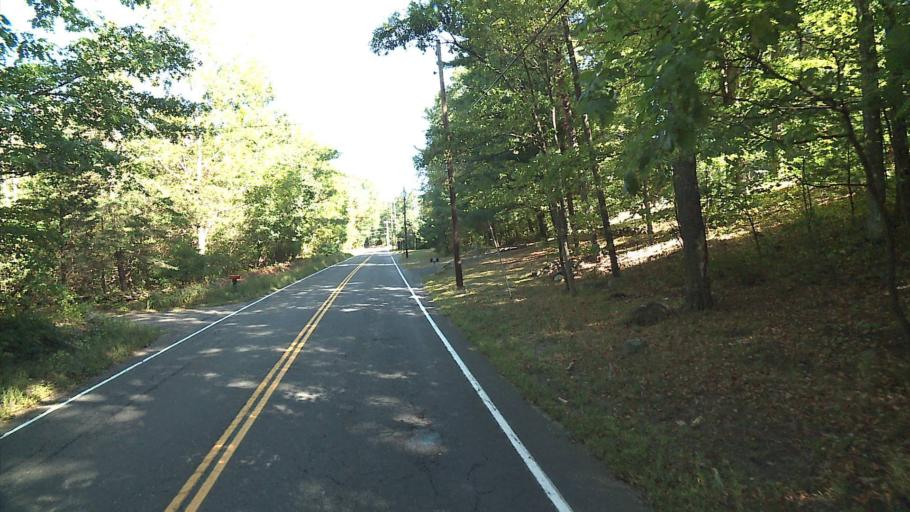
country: US
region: Connecticut
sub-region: Hartford County
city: Bristol
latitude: 41.7182
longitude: -72.9481
